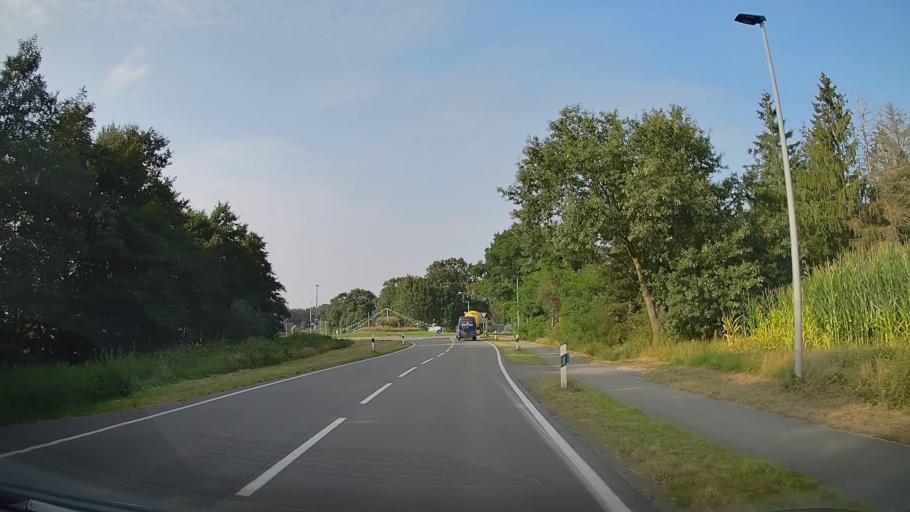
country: DE
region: Lower Saxony
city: Friesoythe
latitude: 53.1087
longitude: 7.8306
